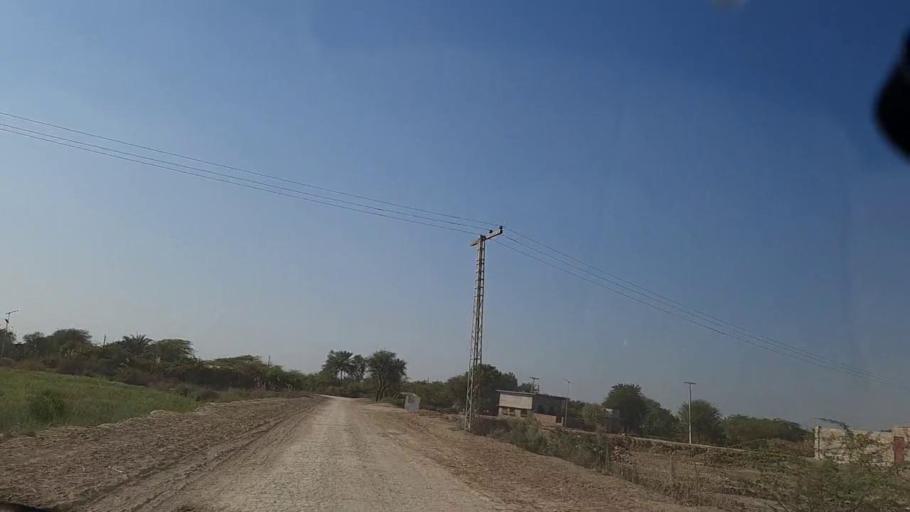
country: PK
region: Sindh
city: Mirpur Khas
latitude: 25.5201
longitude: 68.9267
